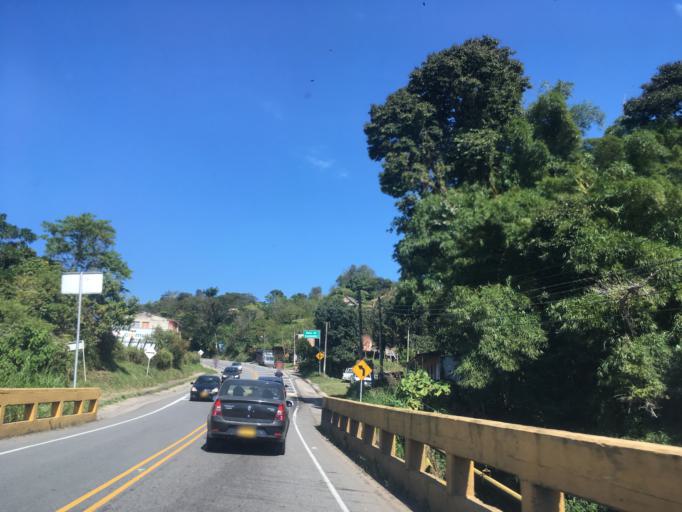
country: CO
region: Santander
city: Suaita
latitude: 6.0652
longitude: -73.4169
